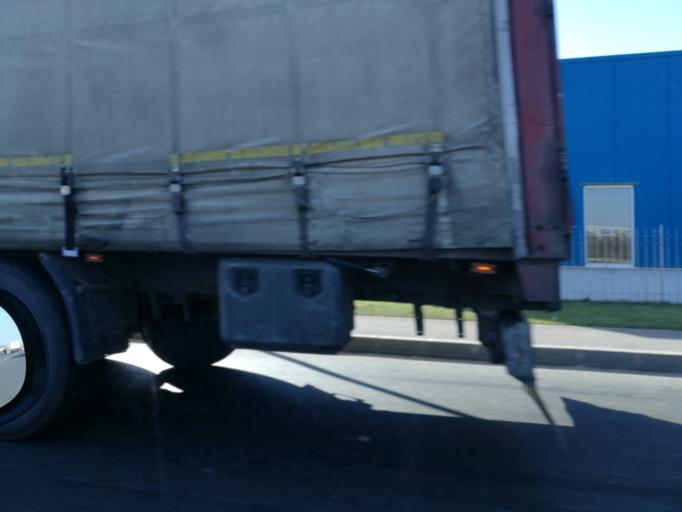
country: RO
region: Ilfov
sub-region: Comuna Chiajna
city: Chiajna
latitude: 44.4389
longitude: 25.9666
